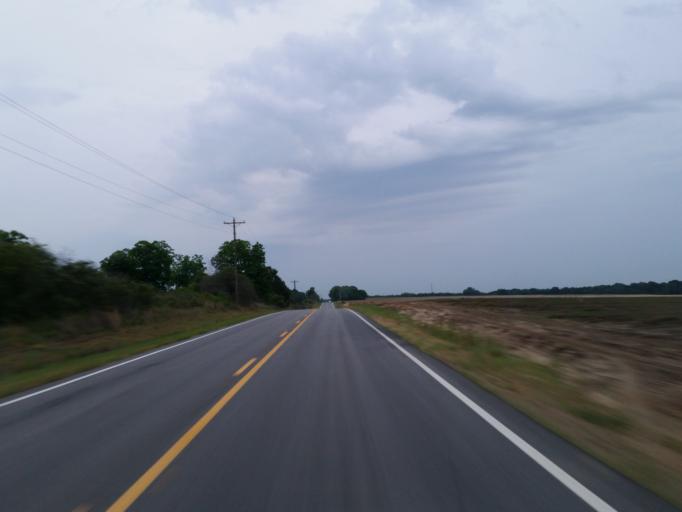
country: US
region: Georgia
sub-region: Turner County
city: Ashburn
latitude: 31.8221
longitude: -83.7326
